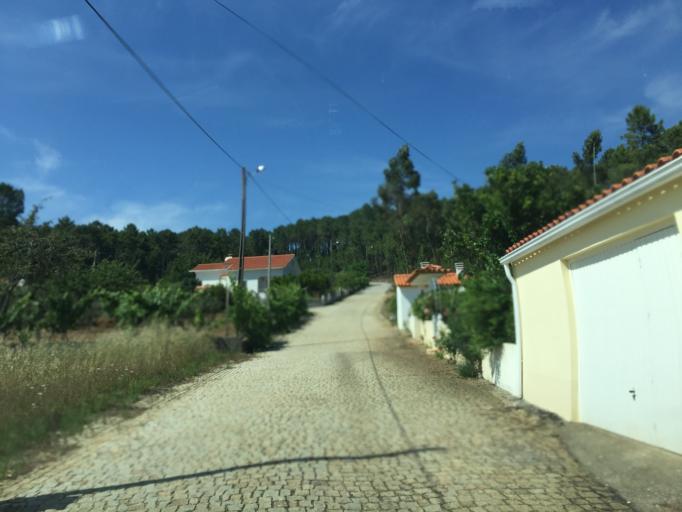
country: PT
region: Castelo Branco
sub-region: Oleiros
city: Oleiros
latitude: 39.9740
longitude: -7.8419
